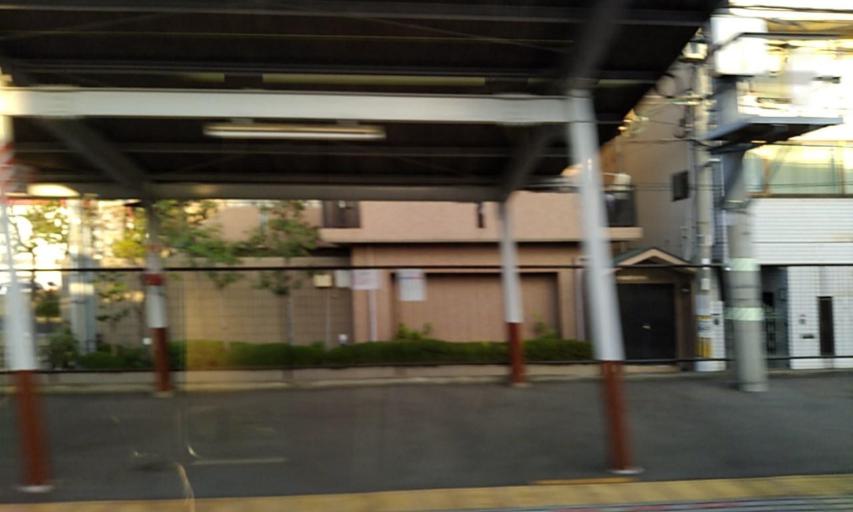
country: JP
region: Osaka
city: Sakai
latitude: 34.5999
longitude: 135.4970
